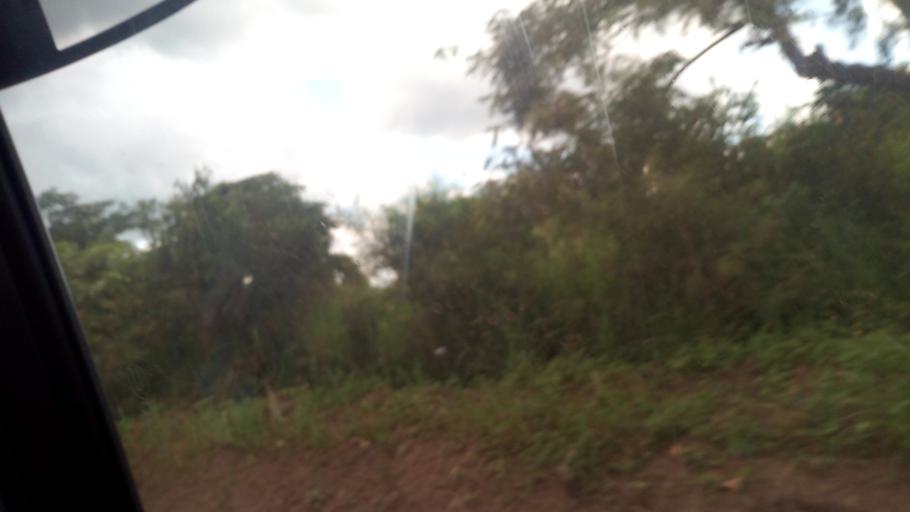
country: UG
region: Western Region
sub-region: Kiryandongo District
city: Kiryandongo
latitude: 1.9311
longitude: 32.1319
